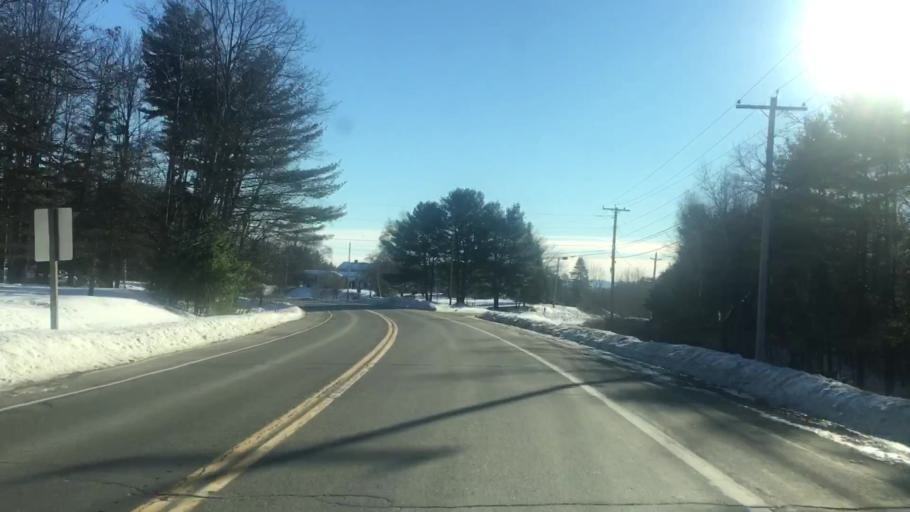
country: US
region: Maine
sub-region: Somerset County
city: Madison
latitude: 44.7836
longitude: -69.8844
